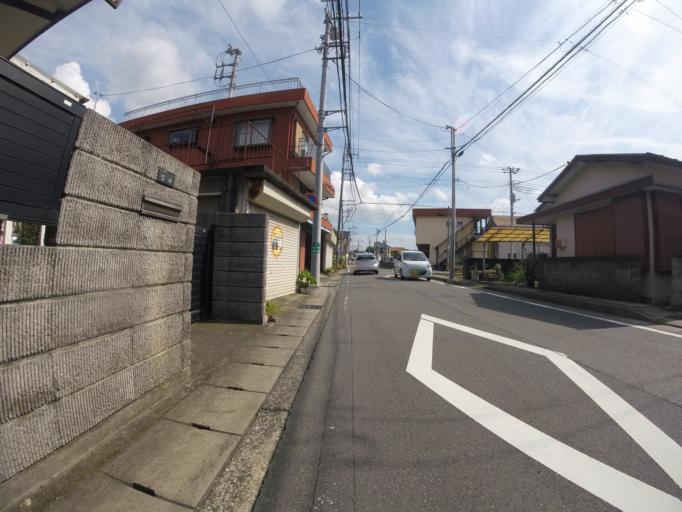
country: JP
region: Shizuoka
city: Mishima
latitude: 35.1172
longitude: 138.9314
